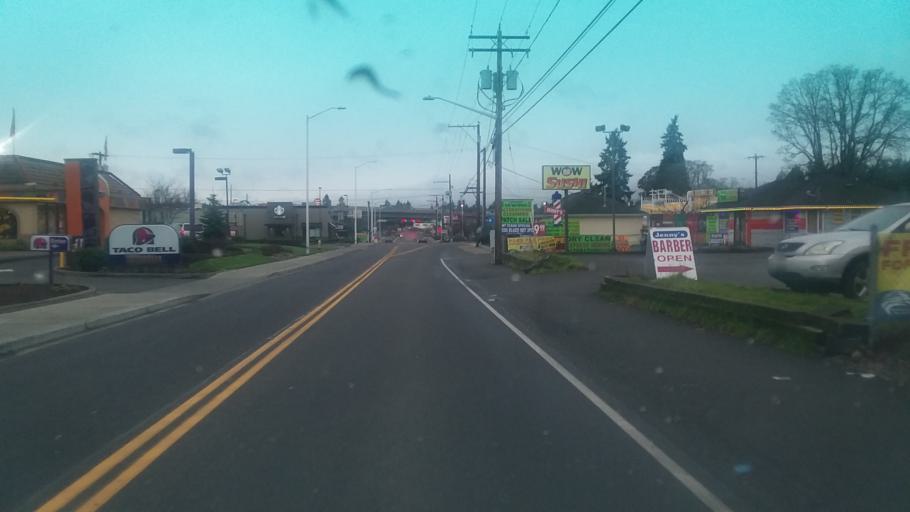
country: US
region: Washington
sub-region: Pierce County
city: Fort Lewis
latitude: 47.1210
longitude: -122.5550
